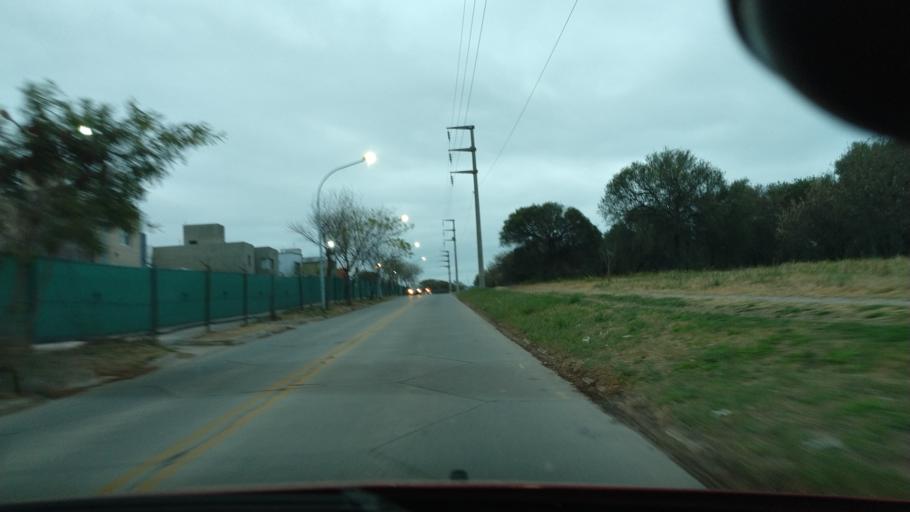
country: AR
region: Cordoba
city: La Calera
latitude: -31.3785
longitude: -64.2738
